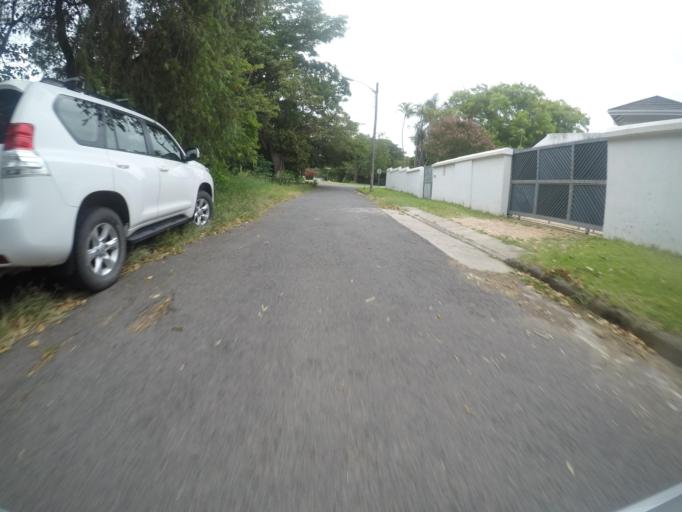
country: ZA
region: Eastern Cape
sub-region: Buffalo City Metropolitan Municipality
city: East London
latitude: -32.9890
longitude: 27.8972
